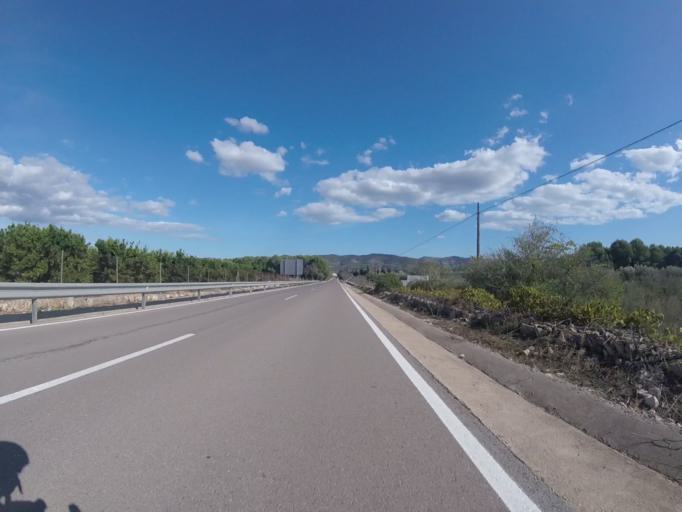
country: ES
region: Valencia
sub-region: Provincia de Castello
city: Alcala de Xivert
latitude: 40.3026
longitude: 0.2086
